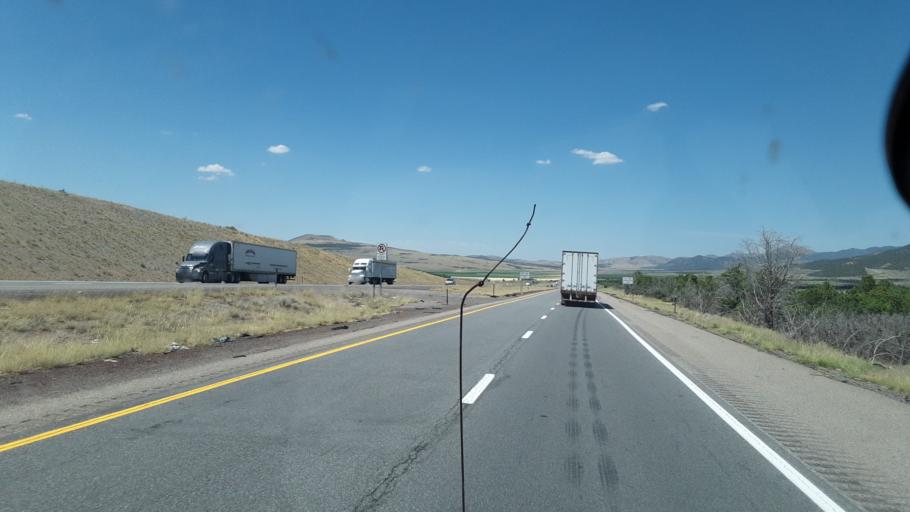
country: US
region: Utah
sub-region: Beaver County
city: Beaver
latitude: 38.4899
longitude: -112.6165
